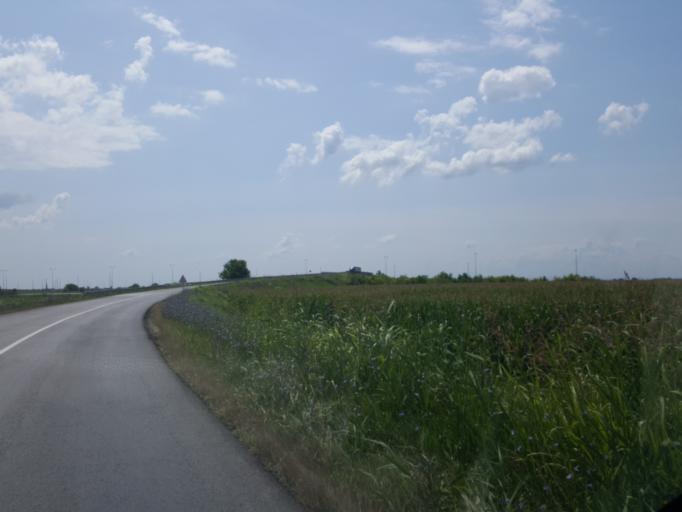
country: RS
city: Ravnje
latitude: 45.0426
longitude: 19.3808
